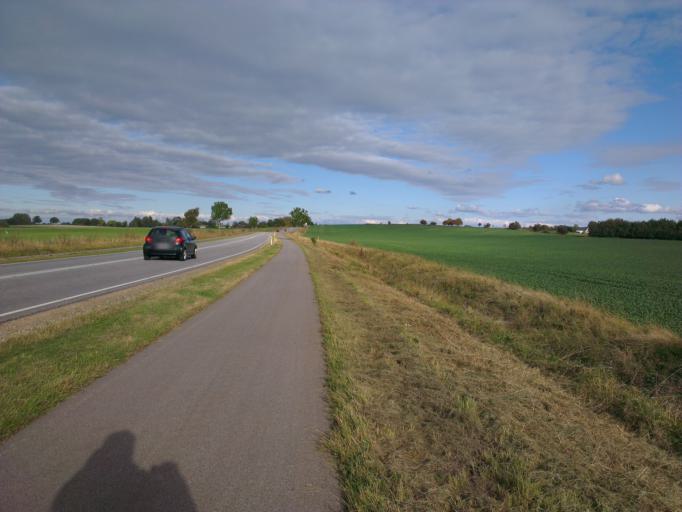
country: DK
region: Capital Region
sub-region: Frederikssund Kommune
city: Skibby
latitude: 55.7165
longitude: 11.9201
